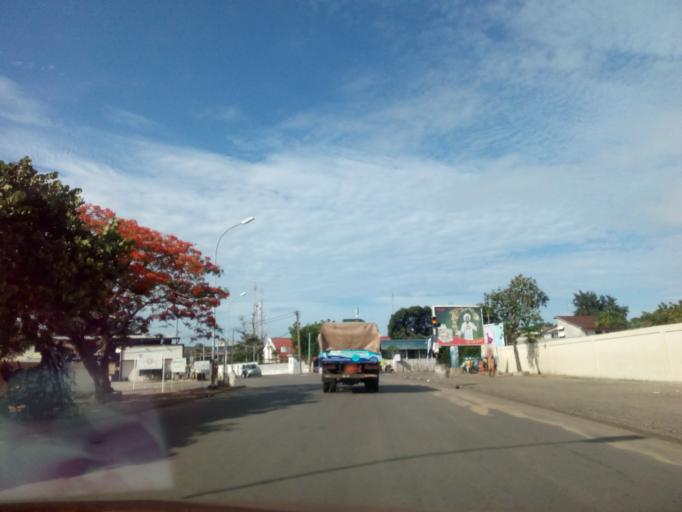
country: BJ
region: Littoral
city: Cotonou
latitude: 6.3567
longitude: 2.4176
